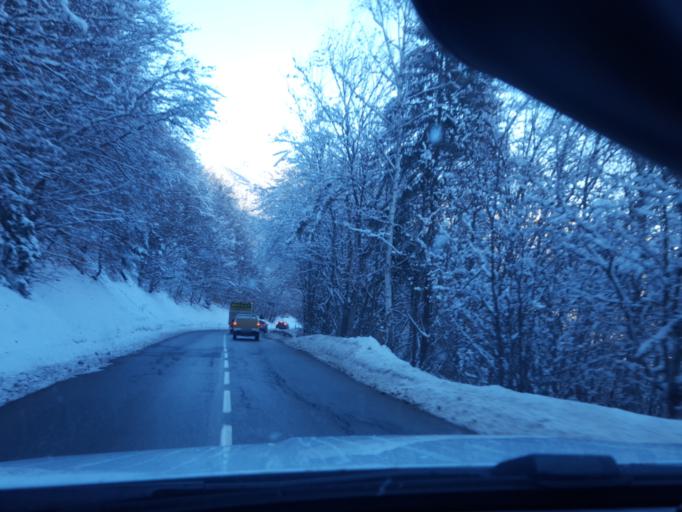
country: FR
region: Rhone-Alpes
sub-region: Departement de la Savoie
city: Salins-les-Thermes
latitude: 45.4697
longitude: 6.5225
